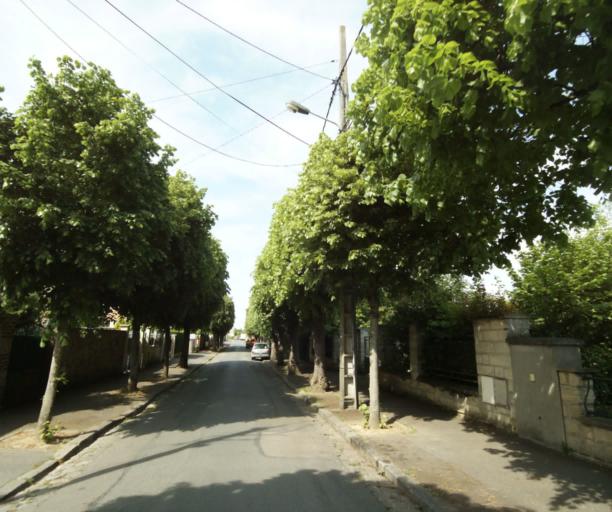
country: FR
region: Ile-de-France
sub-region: Departement des Yvelines
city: Les Mureaux
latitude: 48.9961
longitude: 1.9035
